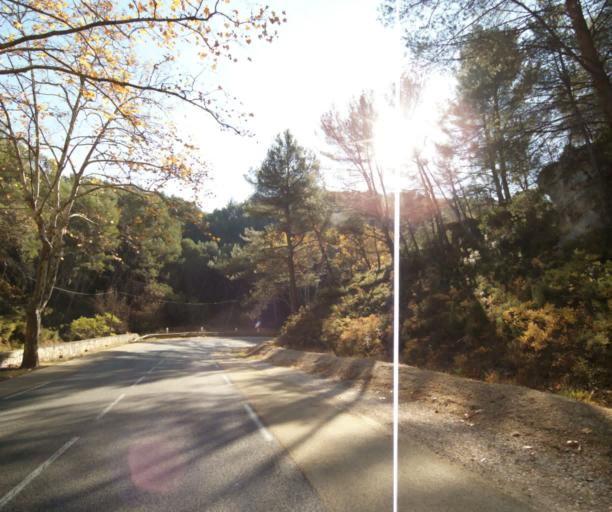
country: FR
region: Provence-Alpes-Cote d'Azur
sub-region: Departement des Bouches-du-Rhone
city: Allauch
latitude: 43.3699
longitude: 5.5049
